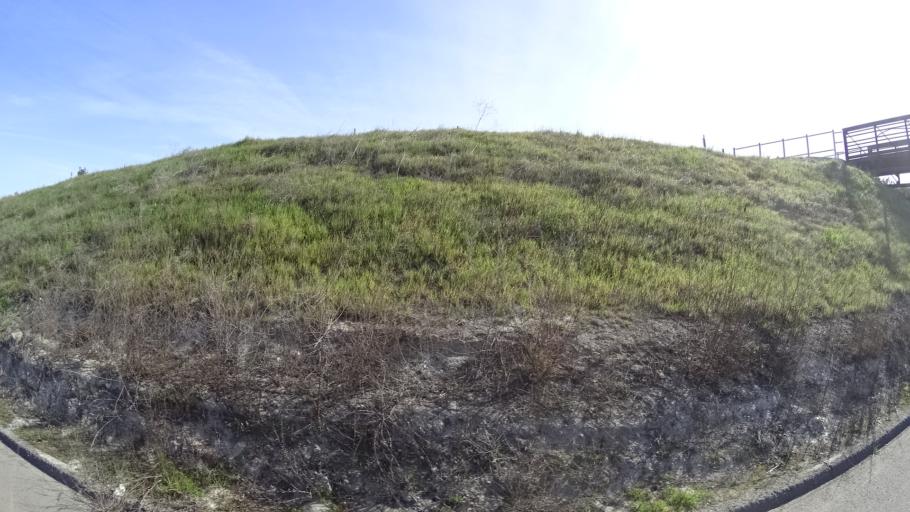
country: US
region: California
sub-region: Fresno County
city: Clovis
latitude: 36.8849
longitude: -119.7783
